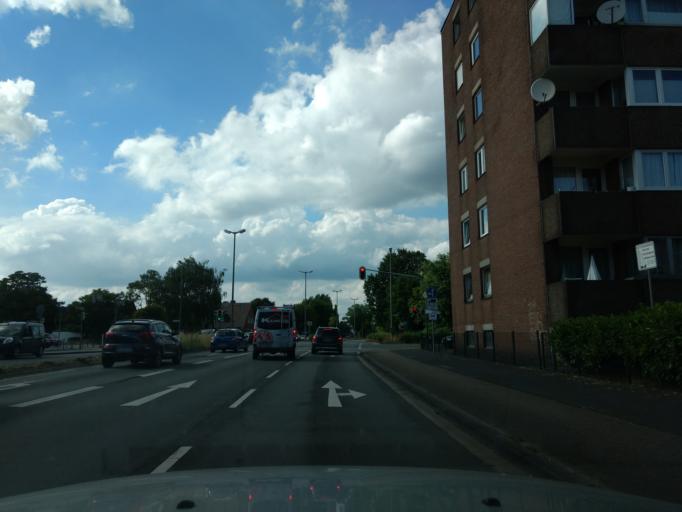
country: DE
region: North Rhine-Westphalia
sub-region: Regierungsbezirk Dusseldorf
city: Neuss
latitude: 51.1855
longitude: 6.6723
